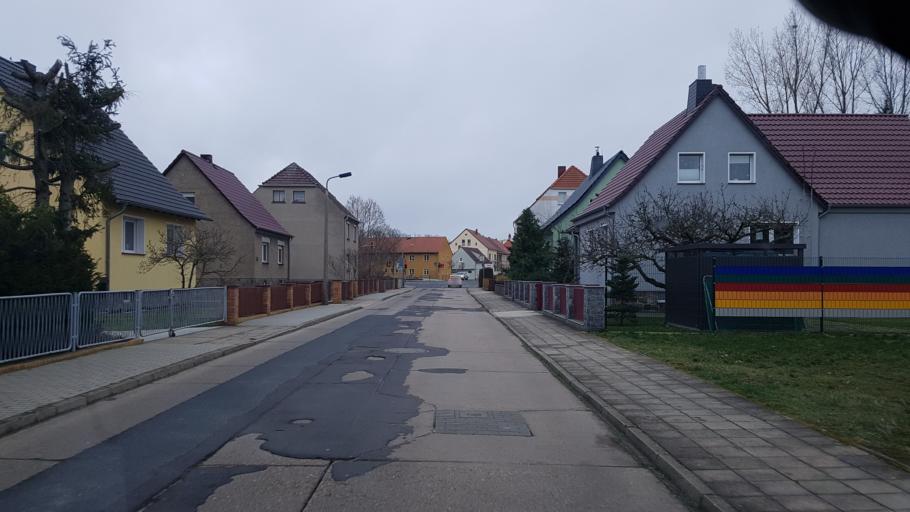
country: DE
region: Brandenburg
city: Herzberg
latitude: 51.6959
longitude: 13.2361
